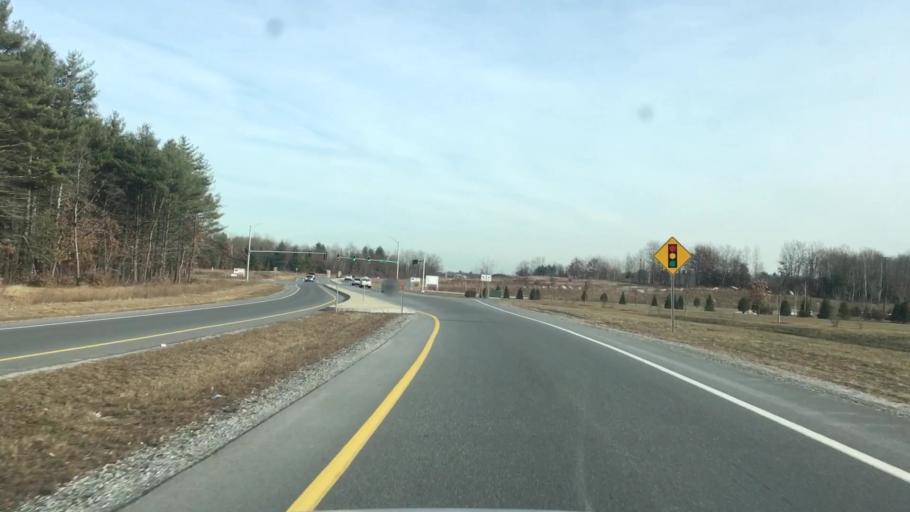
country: US
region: New Hampshire
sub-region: Hillsborough County
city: East Merrimack
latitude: 42.9150
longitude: -71.4404
